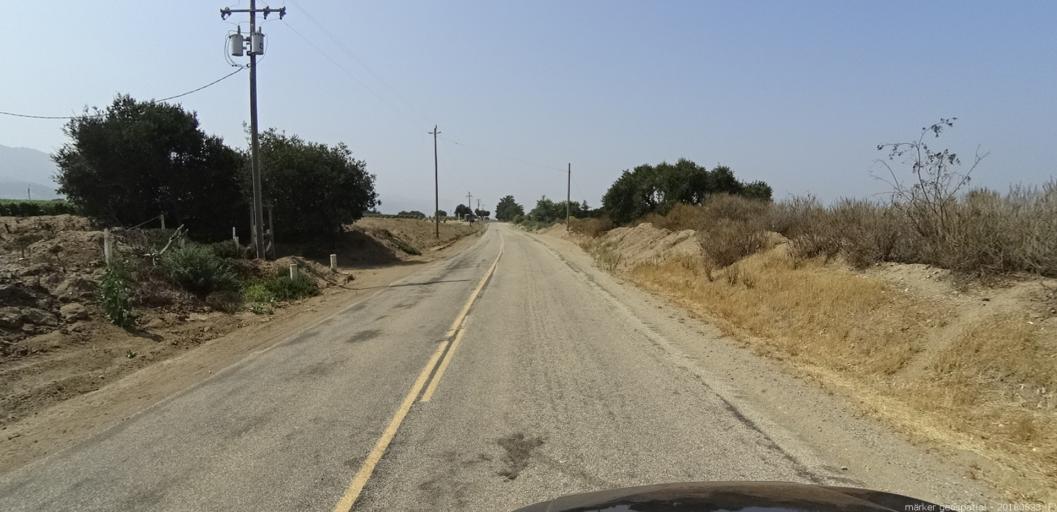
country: US
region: California
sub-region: Monterey County
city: Gonzales
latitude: 36.4524
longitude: -121.4405
